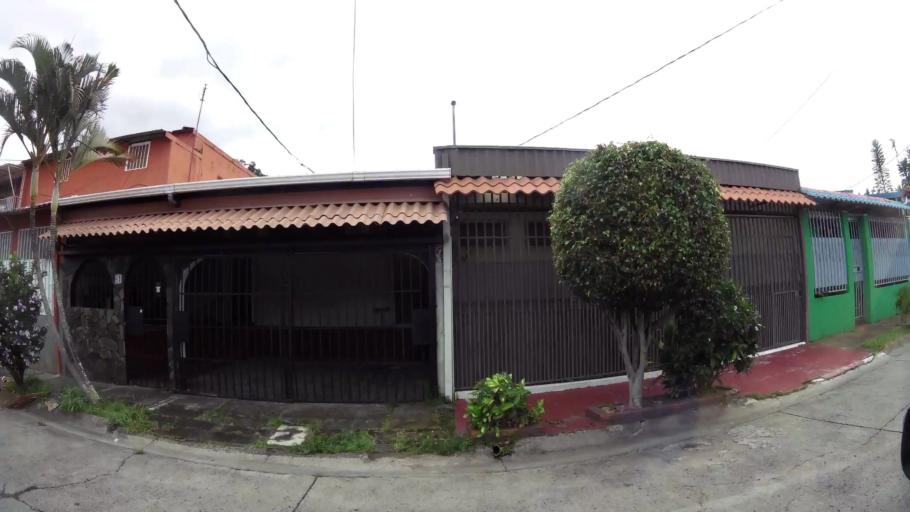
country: CR
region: San Jose
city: Curridabat
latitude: 9.9213
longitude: -84.0400
